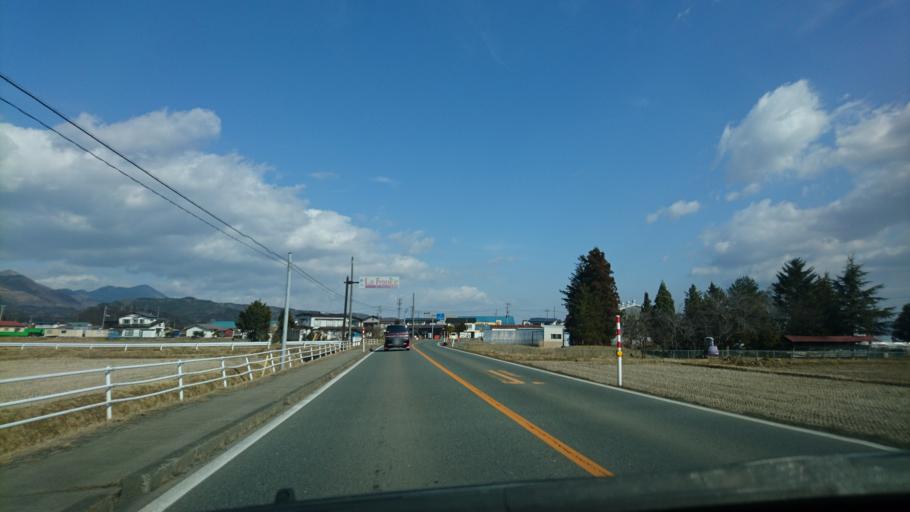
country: JP
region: Iwate
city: Morioka-shi
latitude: 39.5663
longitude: 141.1084
